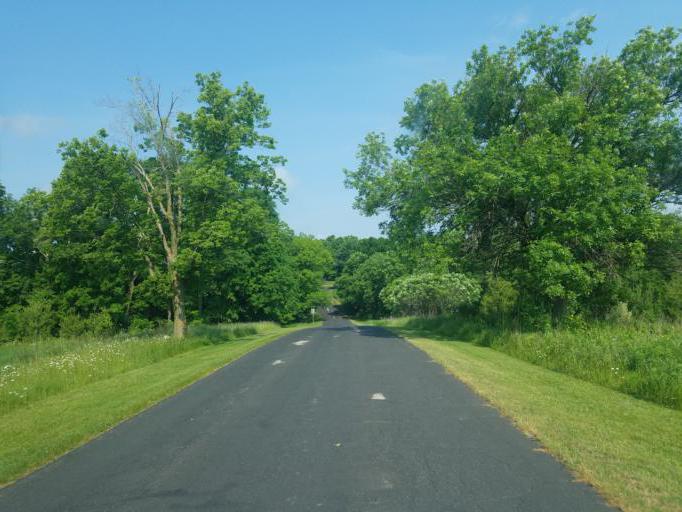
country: US
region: Wisconsin
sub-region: Monroe County
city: Cashton
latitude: 43.7008
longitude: -90.5766
